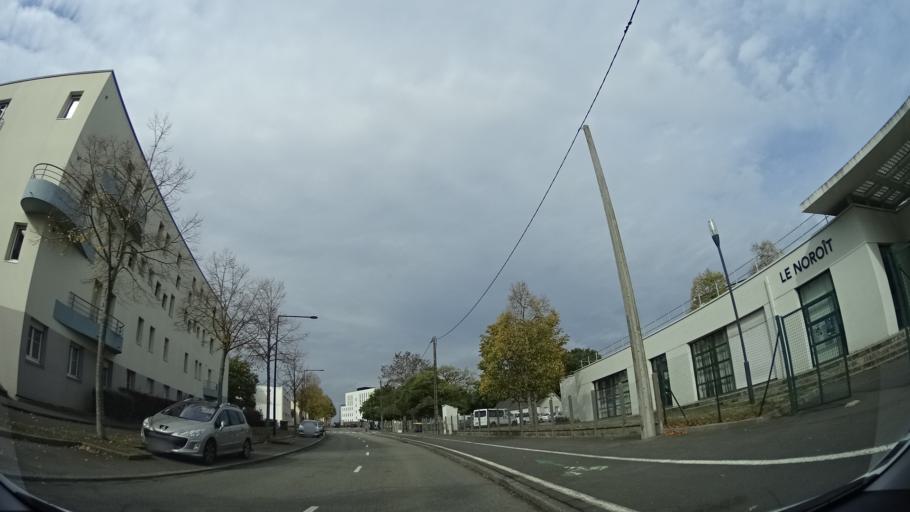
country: FR
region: Brittany
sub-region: Departement d'Ille-et-Vilaine
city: Rennes
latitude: 48.1105
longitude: -1.7109
